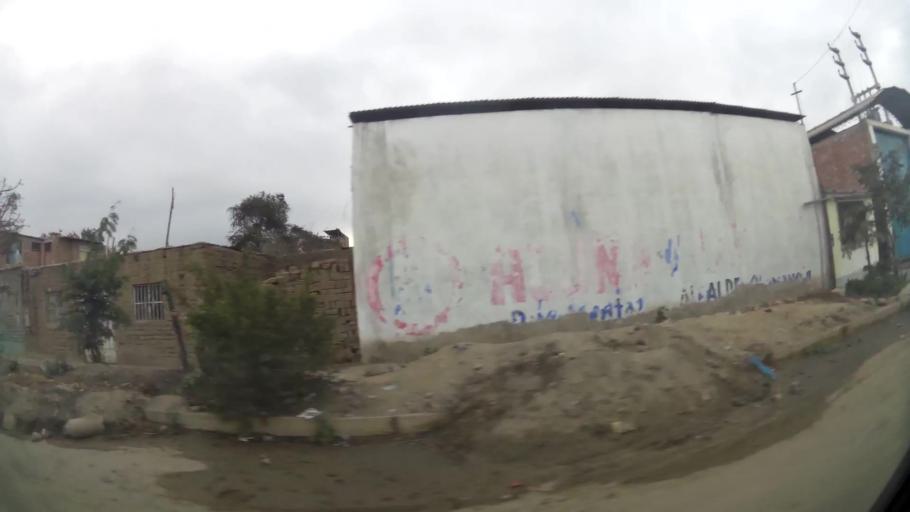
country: PE
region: La Libertad
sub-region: Provincia de Trujillo
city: El Porvenir
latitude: -8.0802
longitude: -79.0145
